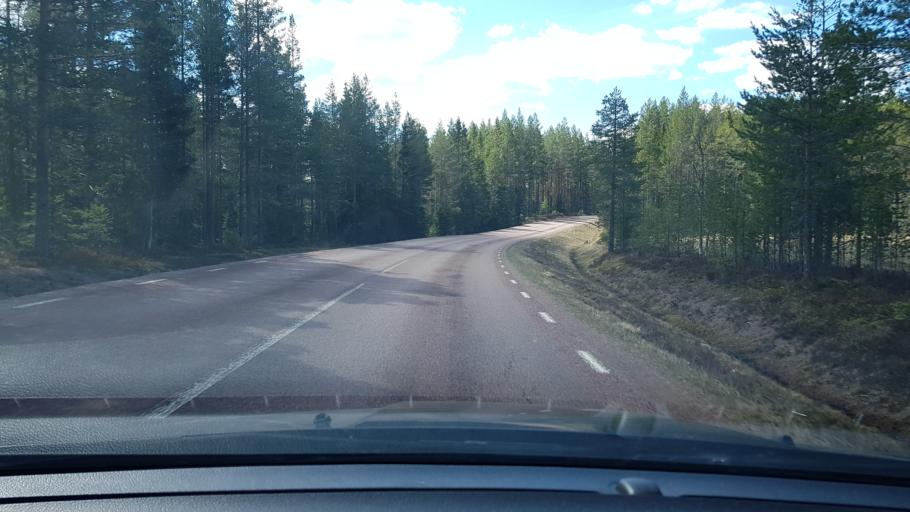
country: SE
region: Dalarna
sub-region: Malung-Saelens kommun
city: Malung
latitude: 61.0583
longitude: 13.4576
